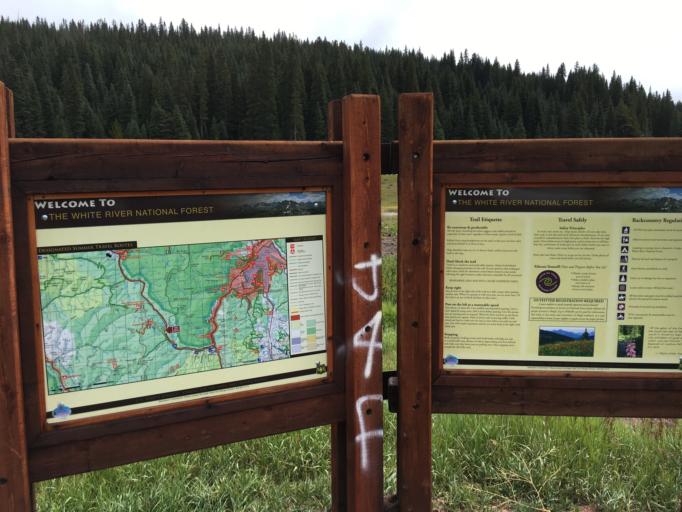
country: US
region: Colorado
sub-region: Summit County
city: Frisco
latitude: 39.5269
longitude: -106.2175
